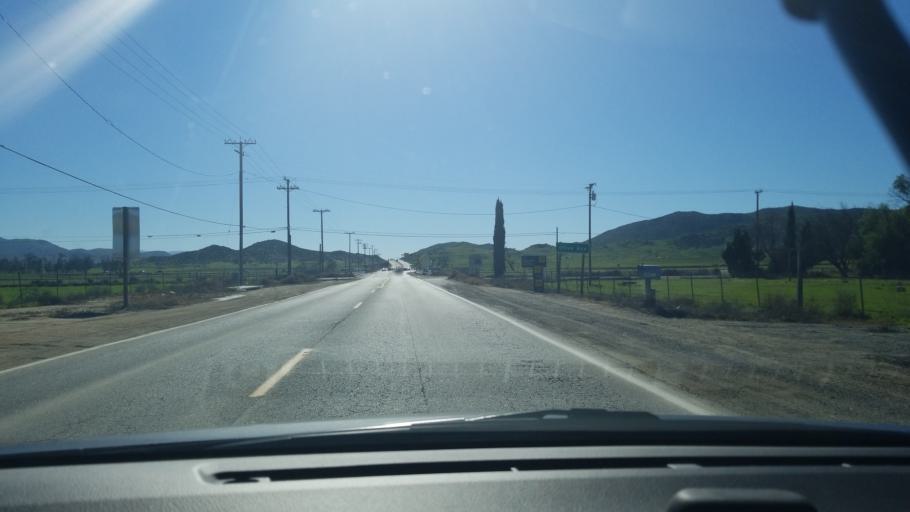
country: US
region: California
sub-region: Riverside County
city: Winchester
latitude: 33.7009
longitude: -117.0849
